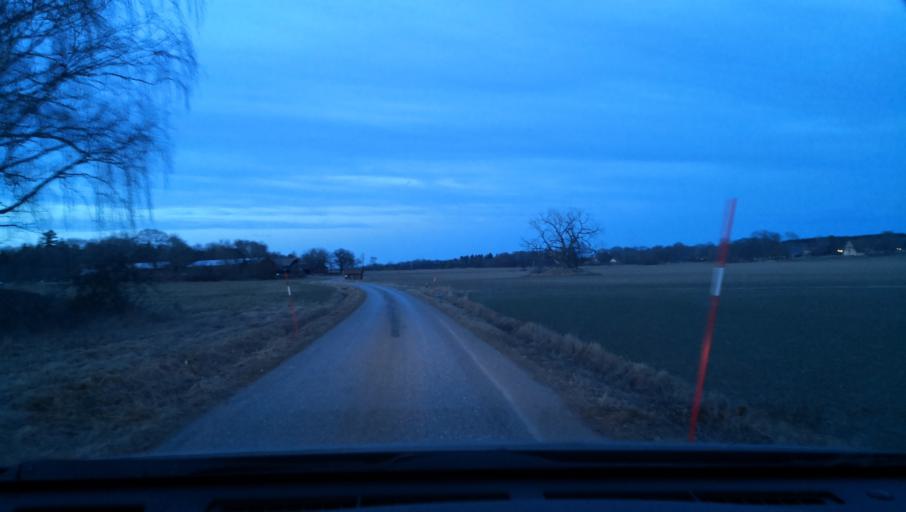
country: SE
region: Uppsala
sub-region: Enkopings Kommun
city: Dalby
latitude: 59.5448
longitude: 17.3649
